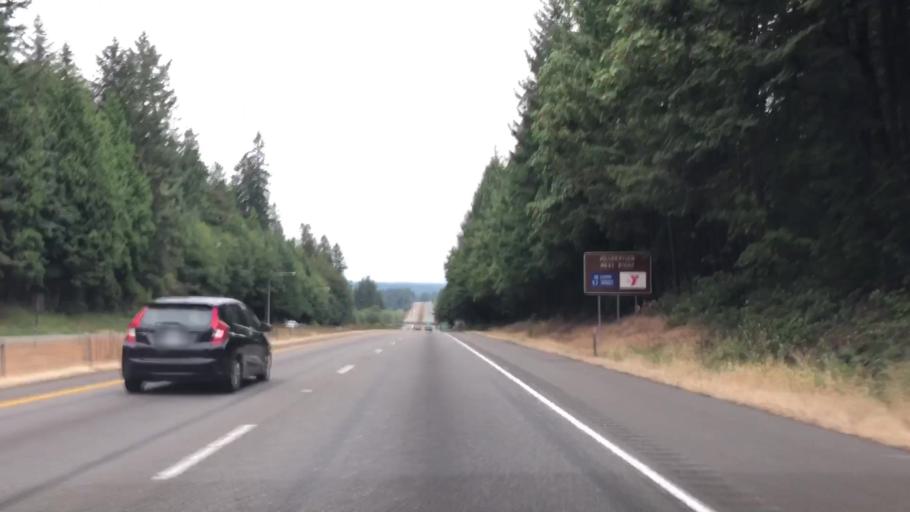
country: US
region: Washington
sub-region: Pierce County
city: Canterwood
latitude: 47.3507
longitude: -122.6109
